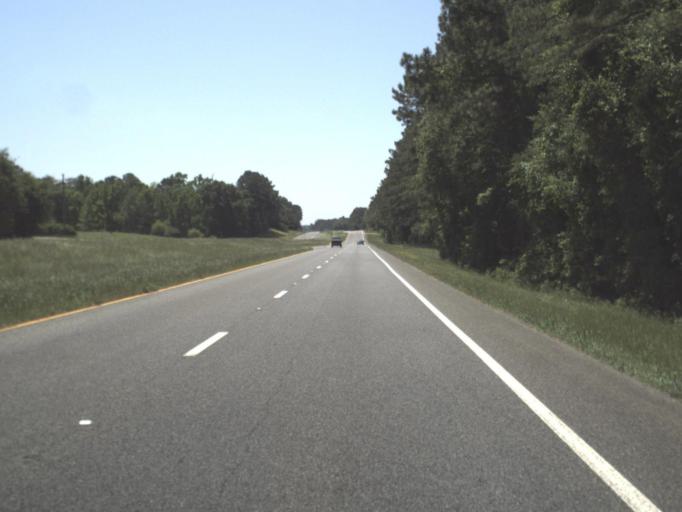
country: US
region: Florida
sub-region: Jefferson County
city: Monticello
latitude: 30.6135
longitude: -83.8724
